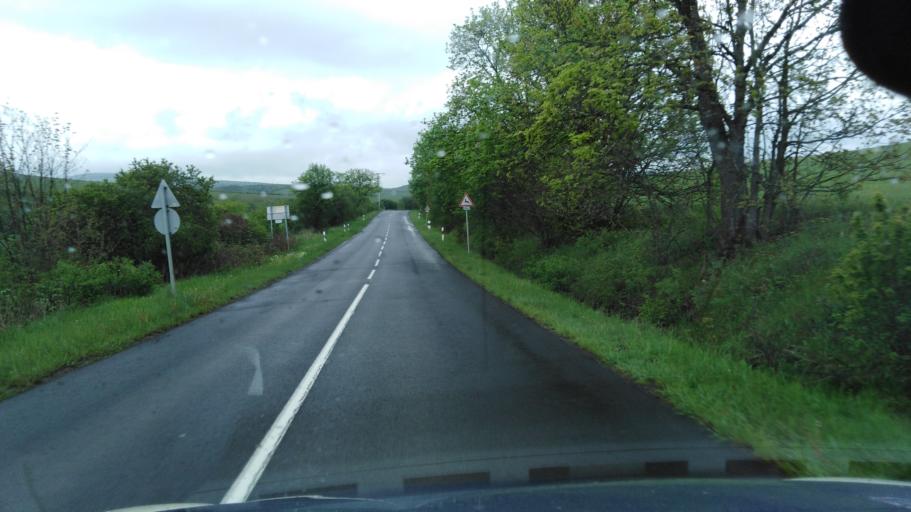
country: HU
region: Nograd
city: Rimoc
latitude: 47.9917
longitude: 19.6148
